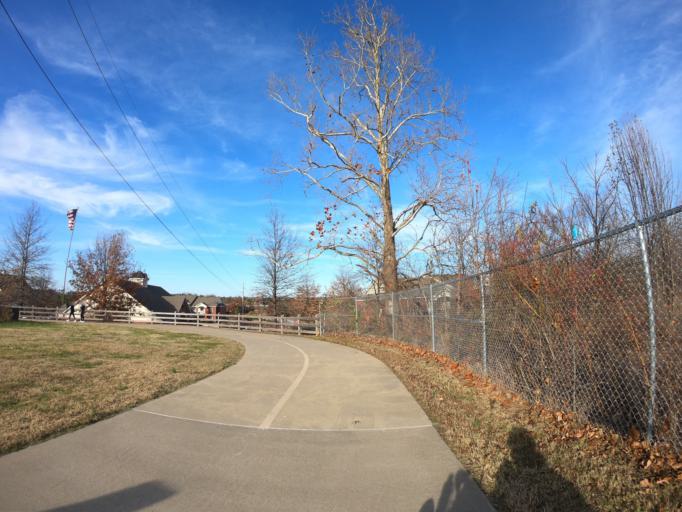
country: US
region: Arkansas
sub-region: Benton County
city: Lowell
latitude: 36.2907
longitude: -94.1652
